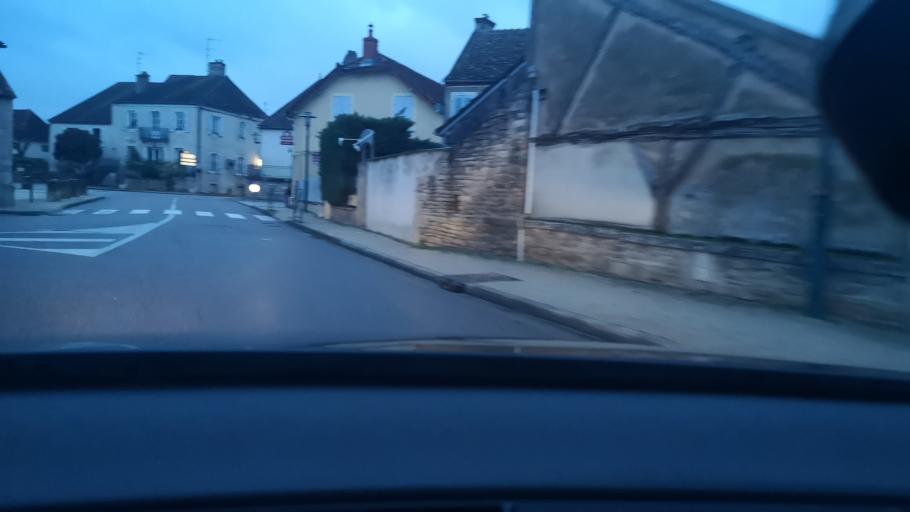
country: FR
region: Bourgogne
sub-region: Departement de Saone-et-Loire
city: Demigny
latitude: 46.9478
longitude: 4.9086
